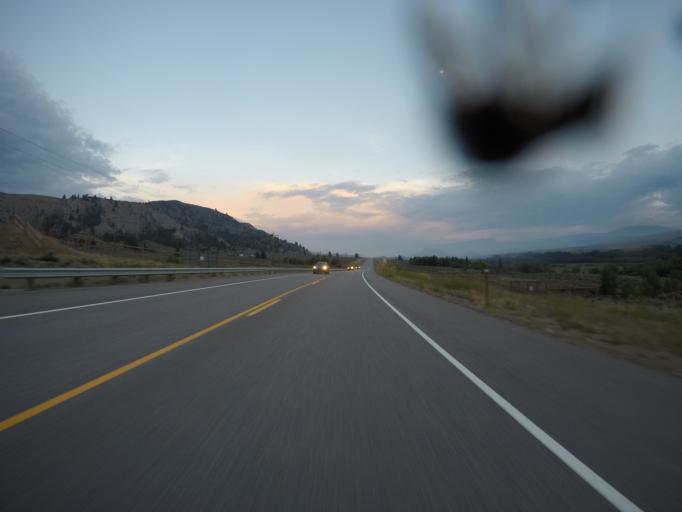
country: US
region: Colorado
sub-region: Grand County
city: Kremmling
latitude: 39.9983
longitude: -106.3660
